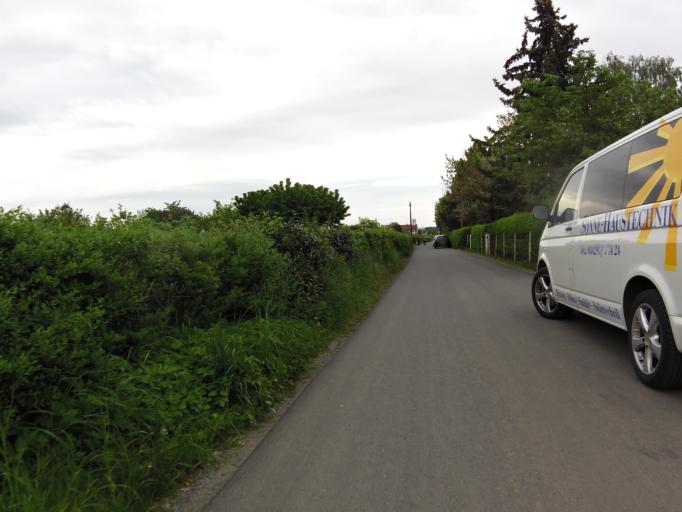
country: DE
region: Saxony
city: Zwenkau
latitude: 51.2771
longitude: 12.3042
